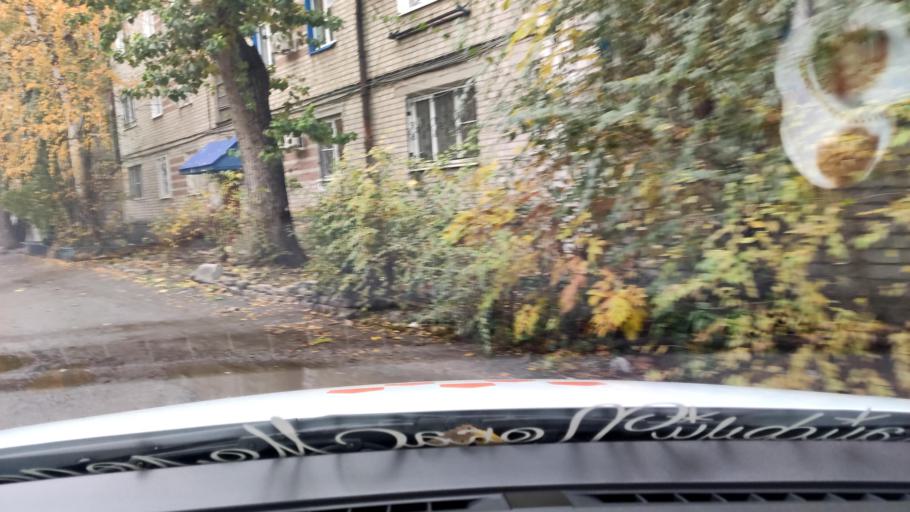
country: RU
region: Voronezj
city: Voronezh
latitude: 51.6873
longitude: 39.1973
